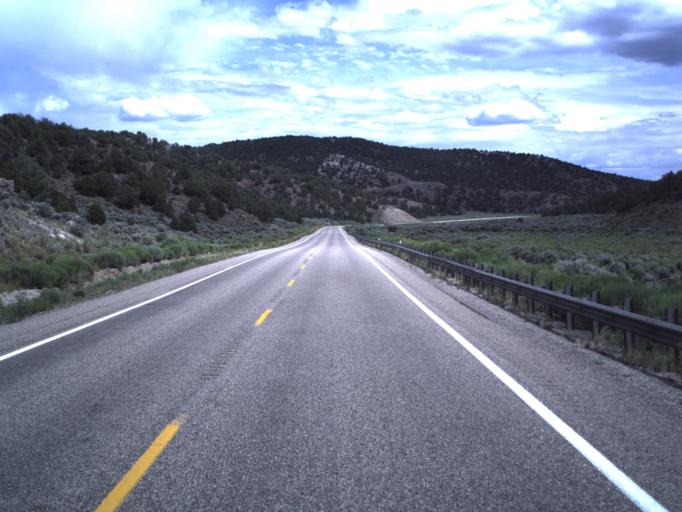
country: US
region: Utah
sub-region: Garfield County
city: Panguitch
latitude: 37.9881
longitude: -112.4965
